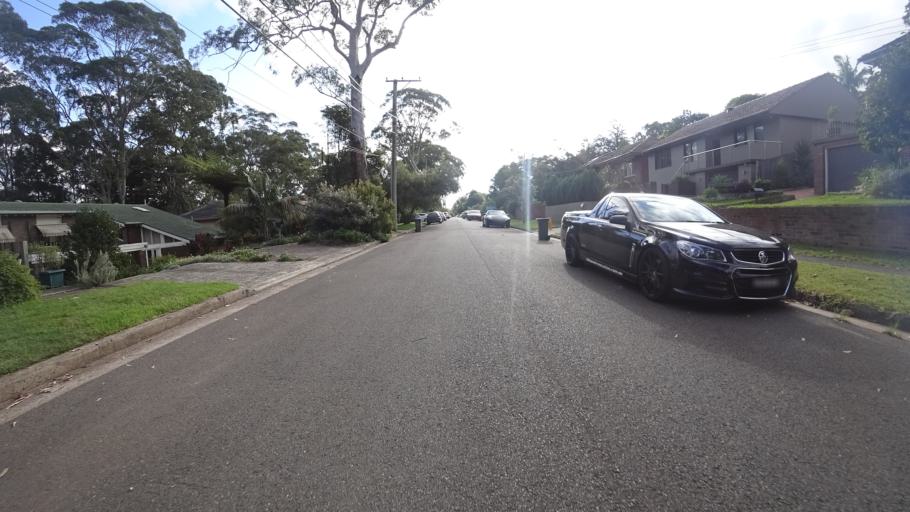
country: AU
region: New South Wales
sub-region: Willoughby
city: Lane Cove North
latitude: -33.8084
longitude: 151.1705
